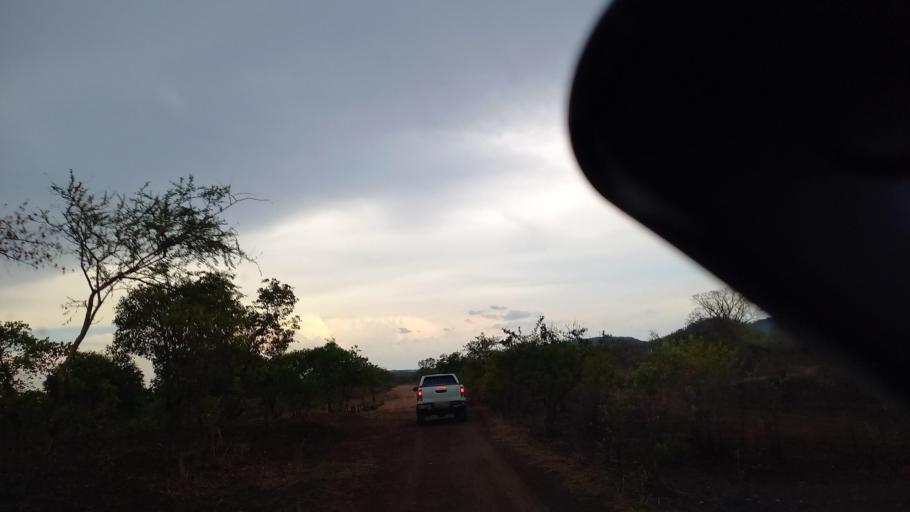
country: ZM
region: Lusaka
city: Kafue
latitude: -16.0302
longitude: 28.3023
